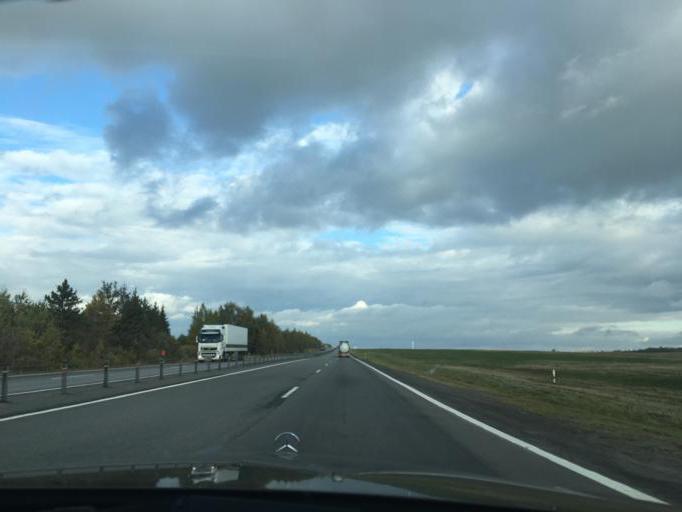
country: BY
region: Vitebsk
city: Dubrowna
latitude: 54.6462
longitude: 30.6081
